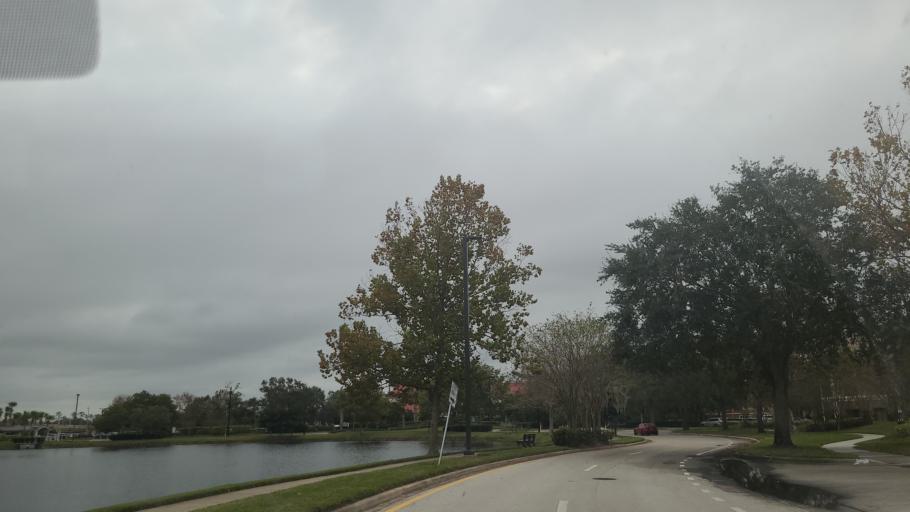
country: US
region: Florida
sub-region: Orange County
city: Conway
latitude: 28.4577
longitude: -81.3071
